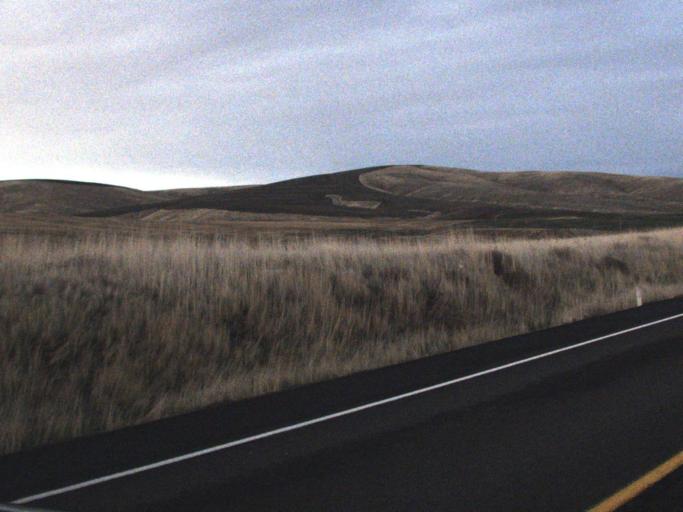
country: US
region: Washington
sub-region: Columbia County
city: Dayton
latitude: 46.5240
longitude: -117.9303
